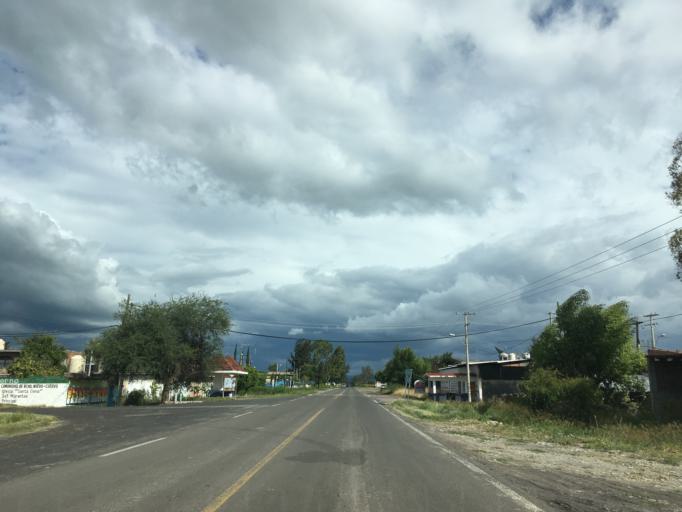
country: MX
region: Michoacan
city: Santa Ana Maya
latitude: 20.0432
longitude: -101.0638
